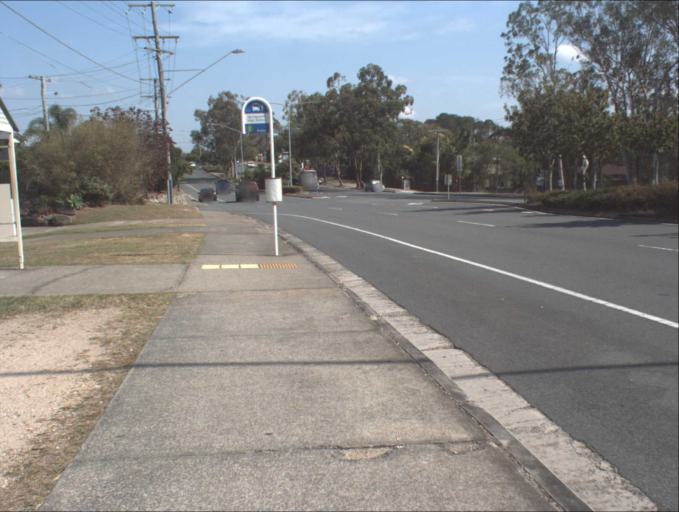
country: AU
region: Queensland
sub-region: Logan
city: Springwood
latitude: -27.6127
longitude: 153.1353
